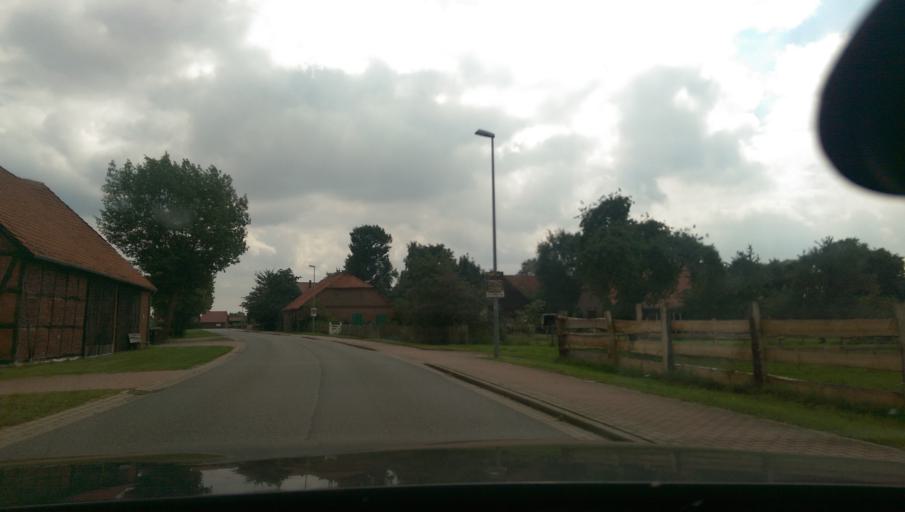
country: DE
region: Lower Saxony
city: Frankenfeld
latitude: 52.6912
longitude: 9.4814
